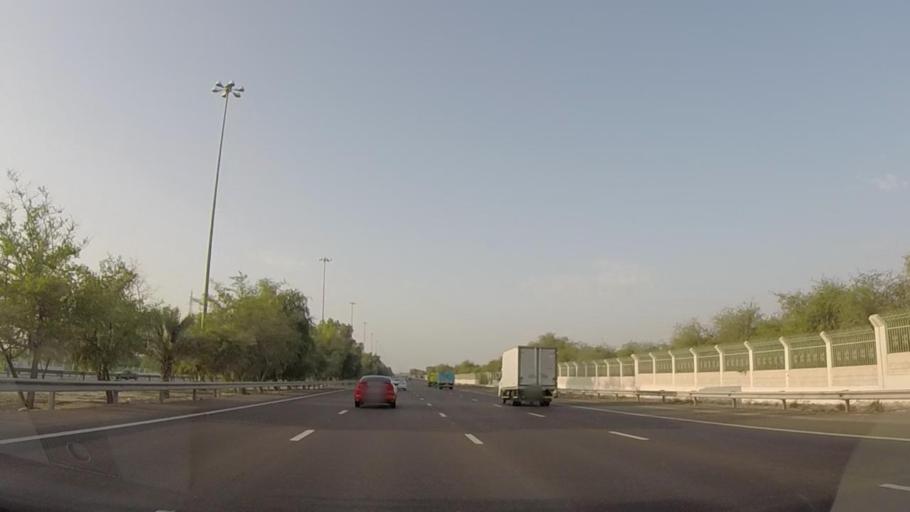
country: AE
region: Dubai
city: Dubai
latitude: 24.8244
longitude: 54.8784
